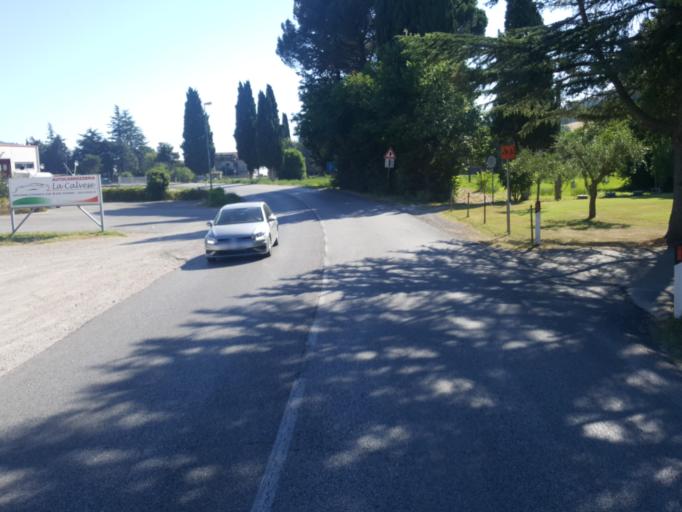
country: IT
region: The Marches
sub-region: Provincia di Pesaro e Urbino
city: Borgo Massano
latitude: 43.8228
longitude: 12.6792
